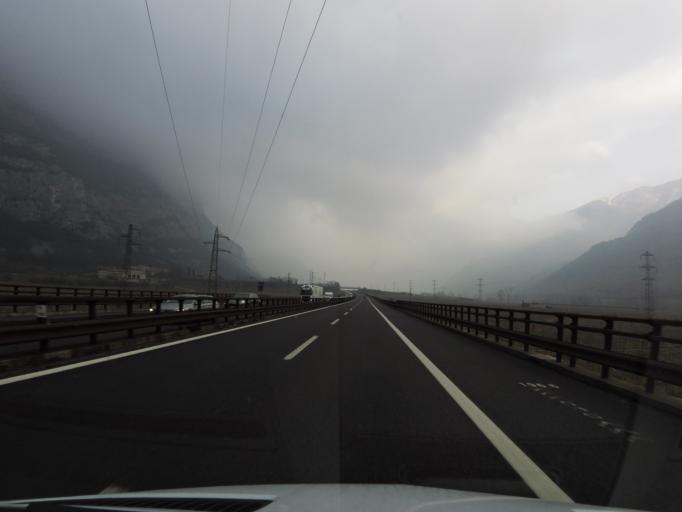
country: IT
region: Veneto
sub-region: Provincia di Verona
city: Dolce
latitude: 45.6190
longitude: 10.8595
